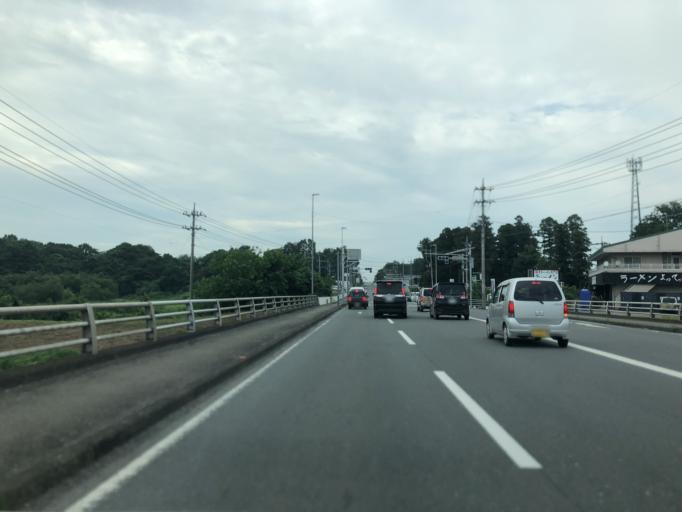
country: JP
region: Saitama
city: Fukiage-fujimi
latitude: 36.0451
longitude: 139.4139
